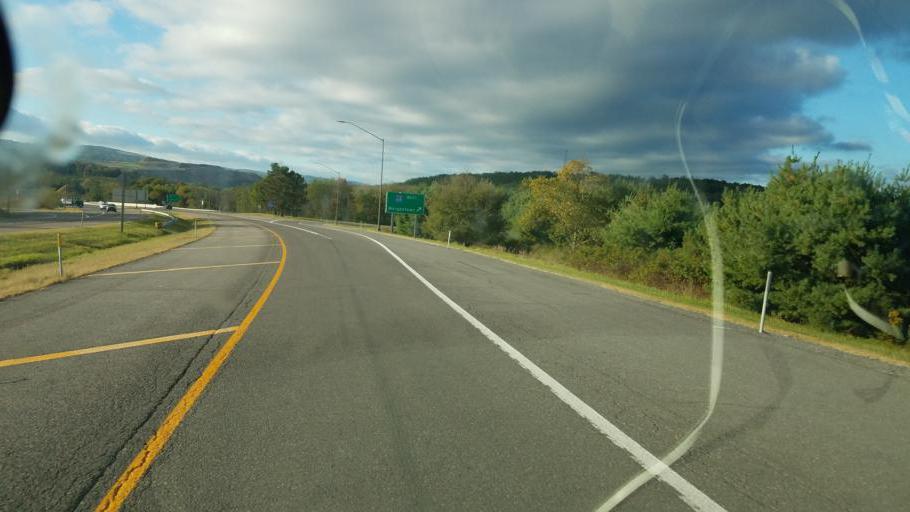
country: US
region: Maryland
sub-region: Allegany County
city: Frostburg
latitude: 39.6357
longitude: -78.9179
